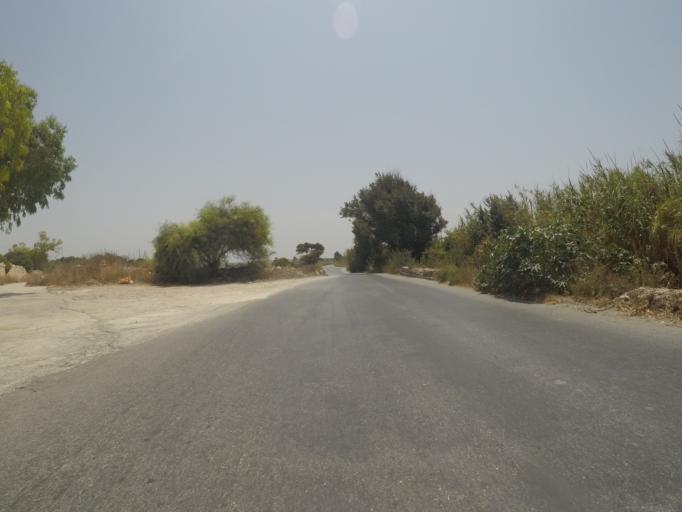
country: MT
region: Ir-Rabat
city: Rabat
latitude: 35.8697
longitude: 14.4144
